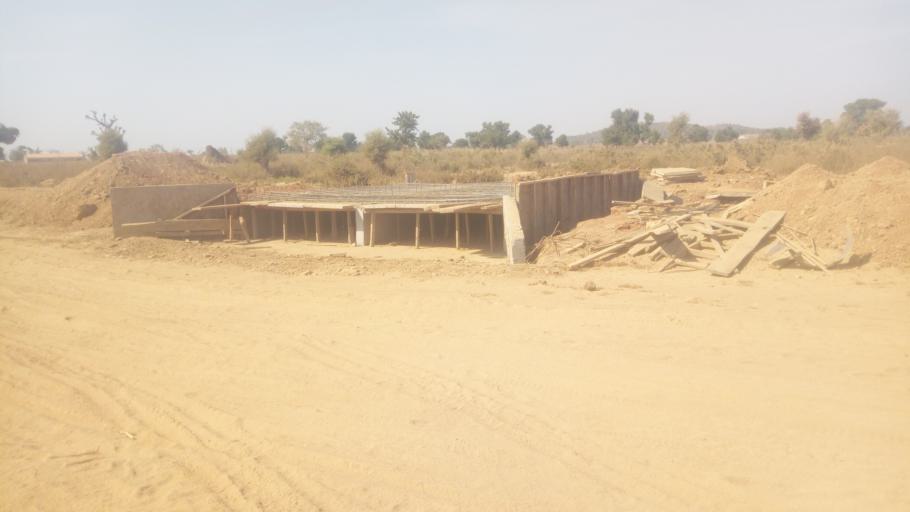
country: NG
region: Adamawa
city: Yola
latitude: 9.2477
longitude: 12.8751
